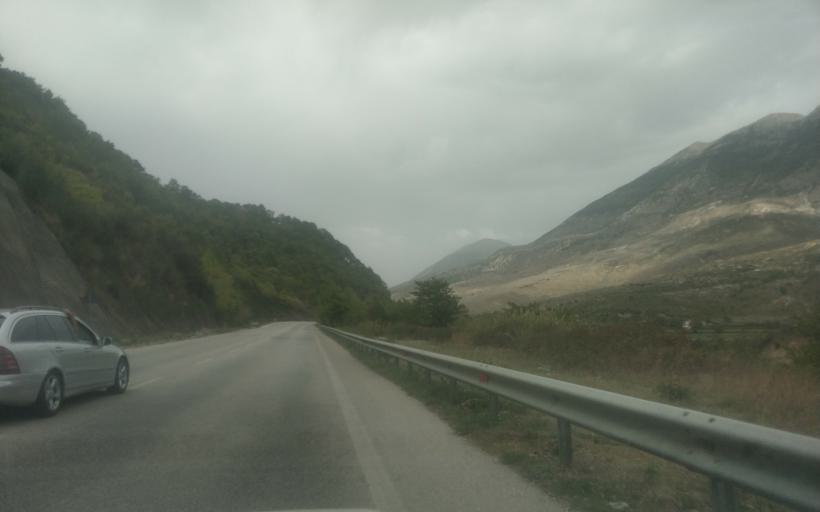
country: AL
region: Gjirokaster
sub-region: Rrethi i Gjirokastres
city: Picar
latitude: 40.2236
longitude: 20.0868
